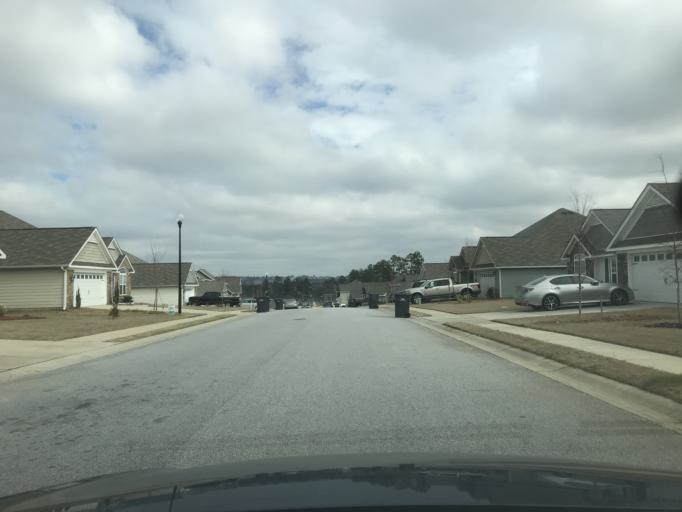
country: US
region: Georgia
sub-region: Columbia County
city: Grovetown
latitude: 33.4435
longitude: -82.1471
